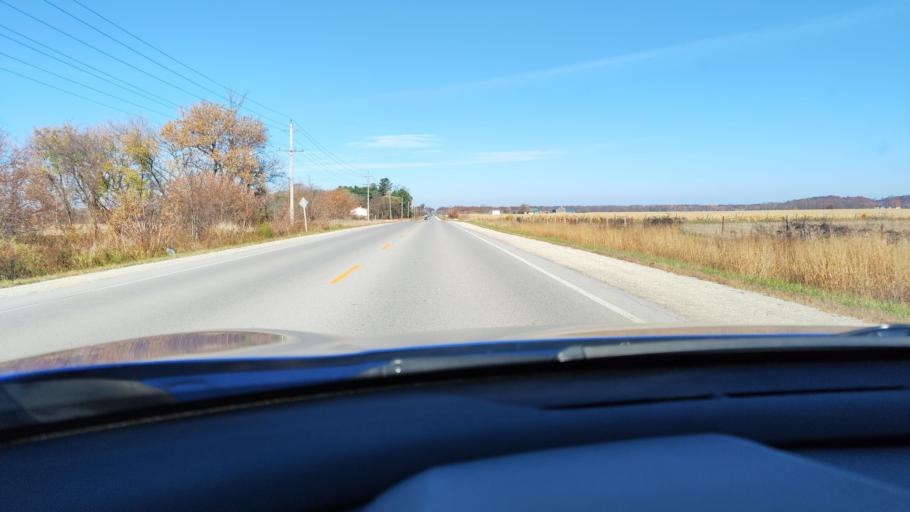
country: CA
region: Ontario
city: Wasaga Beach
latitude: 44.4465
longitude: -80.0690
